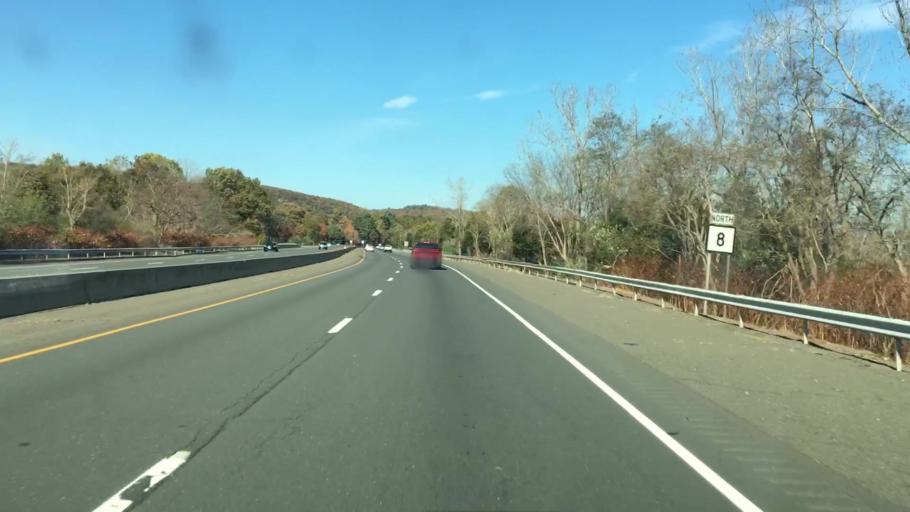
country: US
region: Connecticut
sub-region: New Haven County
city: Seymour
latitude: 41.4315
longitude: -73.0668
